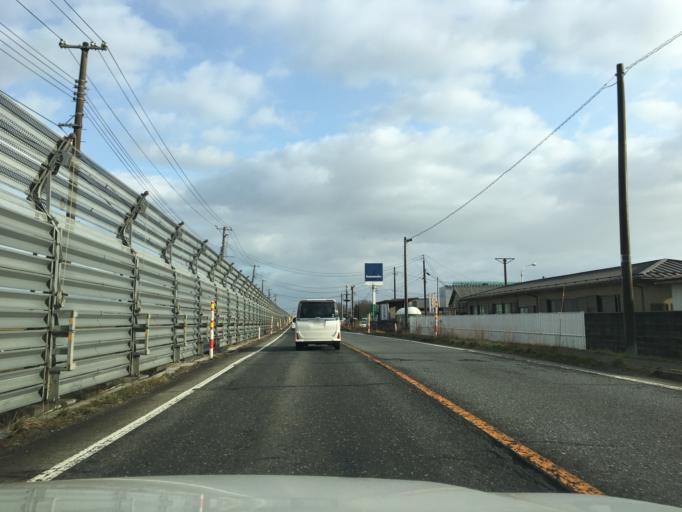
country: JP
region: Yamagata
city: Sakata
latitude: 38.8401
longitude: 139.8488
